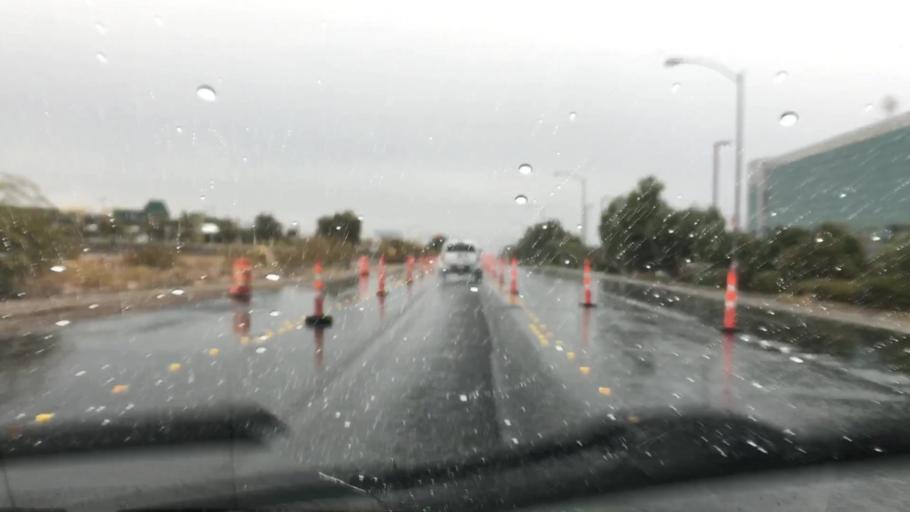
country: US
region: Nevada
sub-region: Clark County
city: Paradise
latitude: 36.0666
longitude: -115.1634
